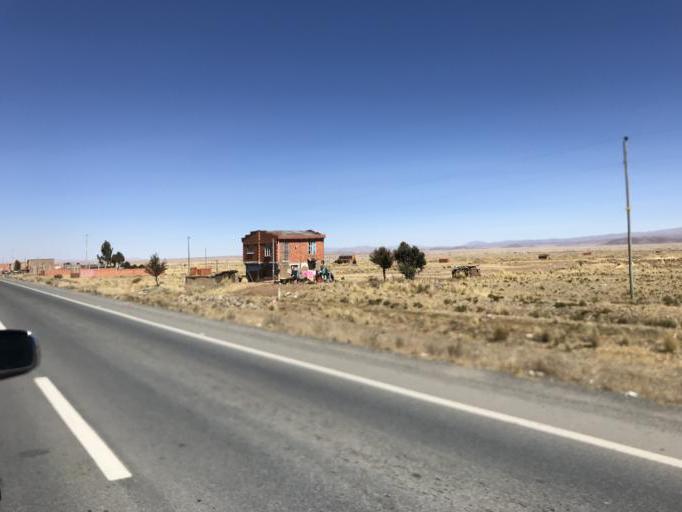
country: BO
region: La Paz
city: Batallas
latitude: -16.3736
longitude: -68.3830
